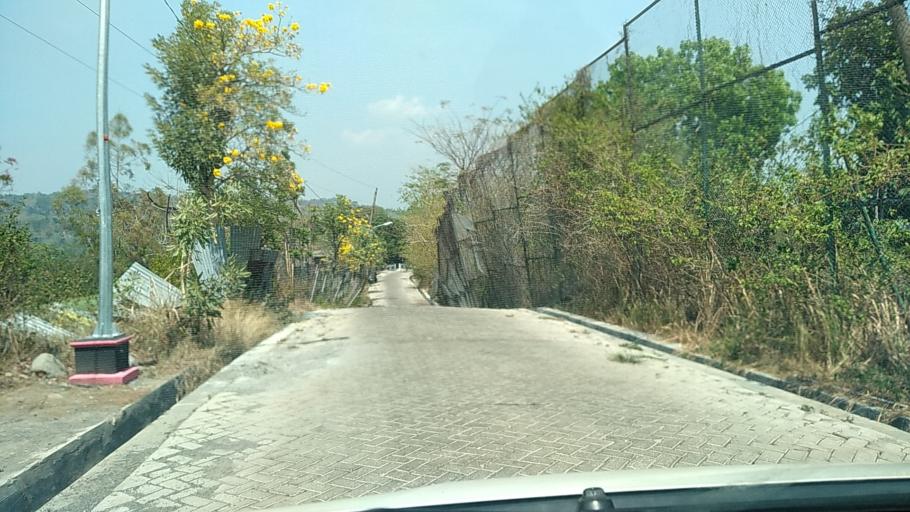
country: ID
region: Central Java
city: Semarang
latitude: -7.0353
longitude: 110.4112
